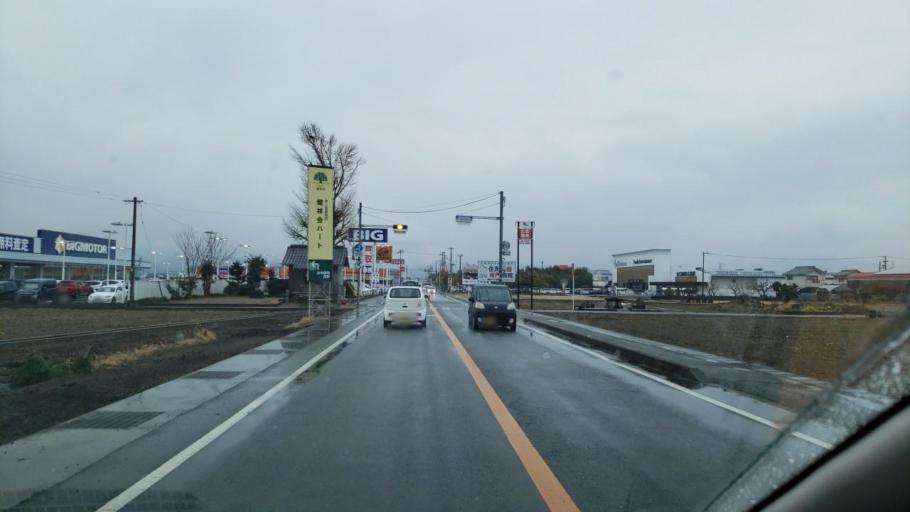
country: JP
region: Tokushima
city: Ishii
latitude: 34.1118
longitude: 134.4365
